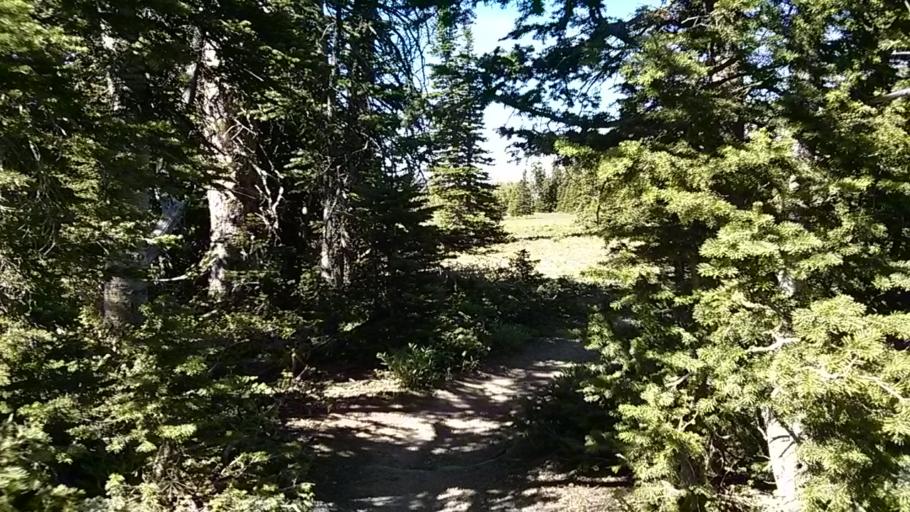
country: US
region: Utah
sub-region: Iron County
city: Parowan
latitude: 37.6354
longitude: -112.8239
